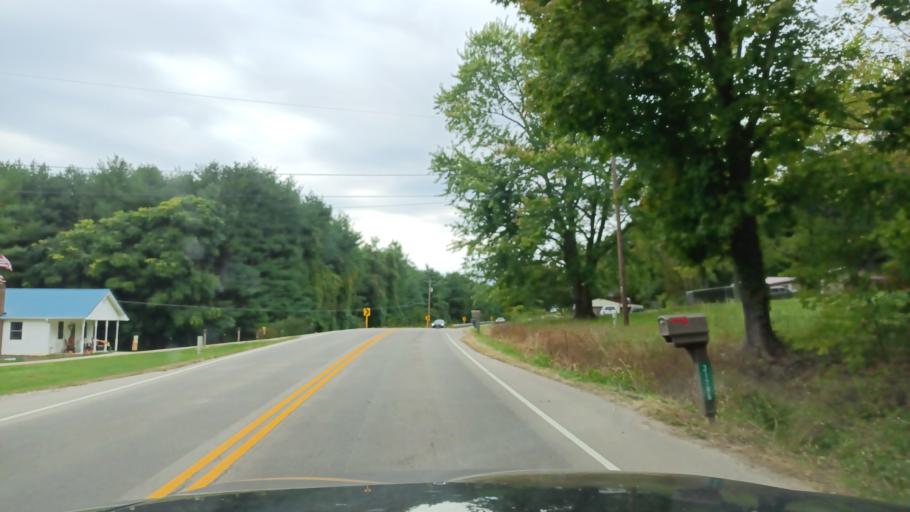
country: US
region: Ohio
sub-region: Ross County
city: Chillicothe
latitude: 39.2839
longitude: -82.8591
